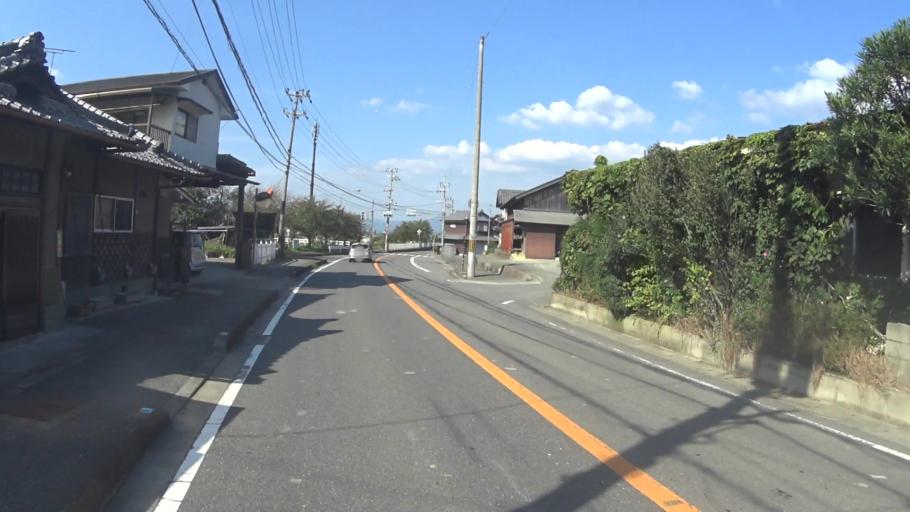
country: JP
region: Kyoto
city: Kameoka
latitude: 34.9892
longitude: 135.5466
